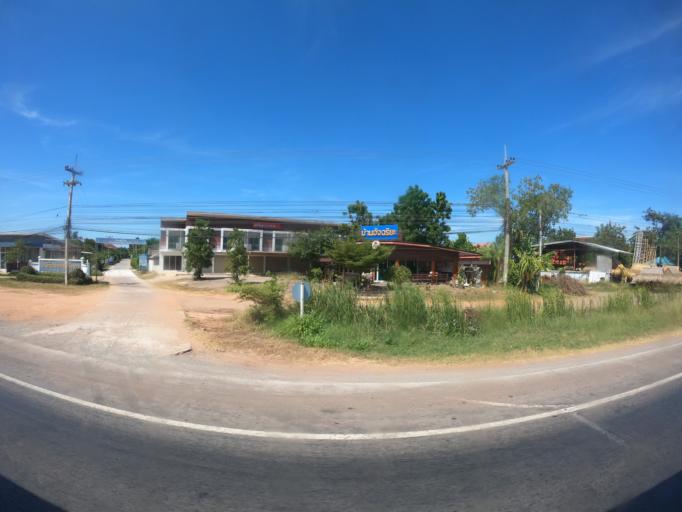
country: TH
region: Nakhon Ratchasima
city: Non Sung
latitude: 15.1688
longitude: 102.3343
